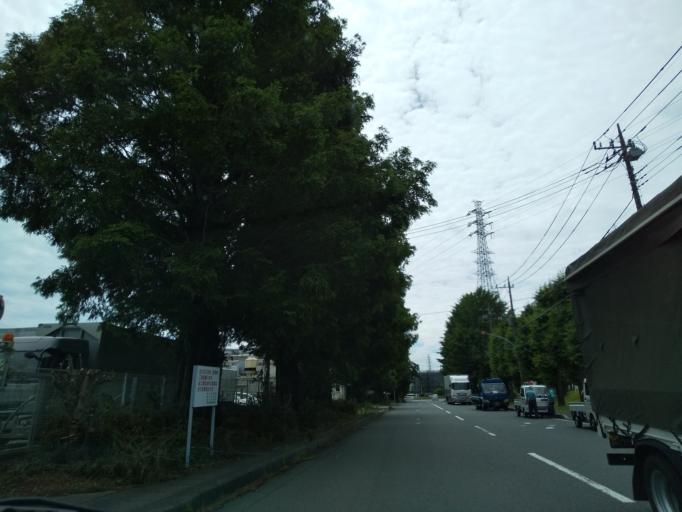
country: JP
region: Kanagawa
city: Zama
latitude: 35.5104
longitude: 139.3454
